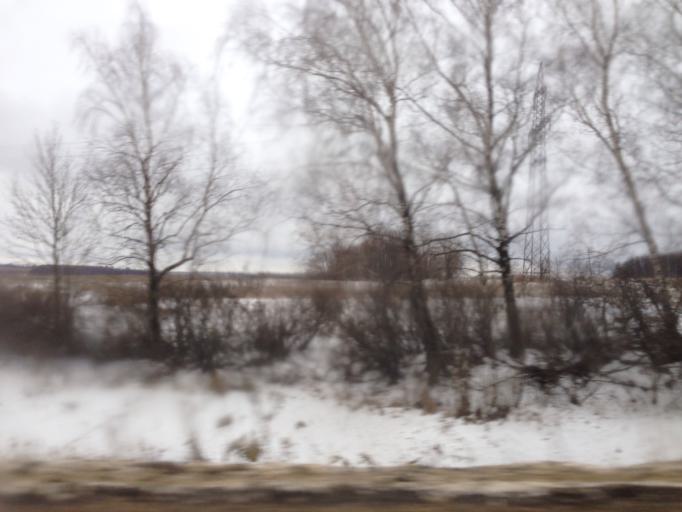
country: RU
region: Tula
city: Skuratovskiy
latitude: 54.1193
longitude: 37.7066
